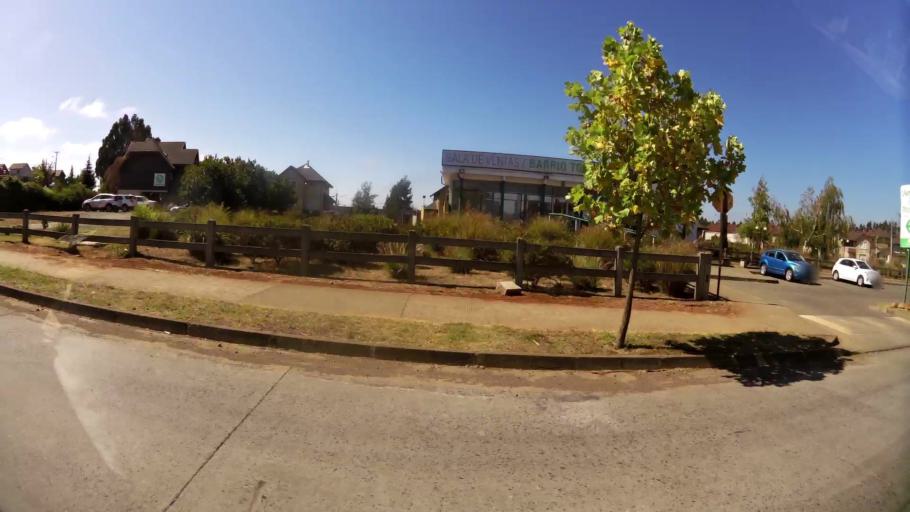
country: CL
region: Biobio
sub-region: Provincia de Concepcion
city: Concepcion
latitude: -36.7856
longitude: -73.0380
